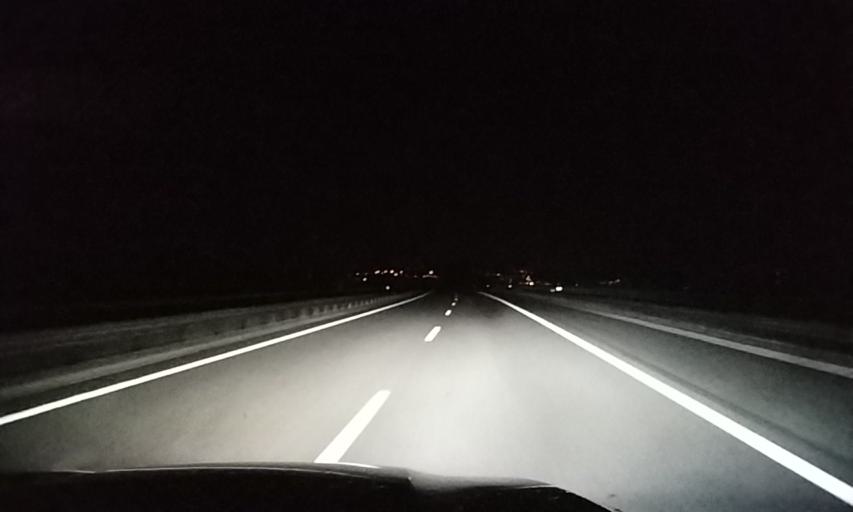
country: PT
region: Coimbra
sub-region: Coimbra
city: Coimbra
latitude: 40.2157
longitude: -8.4869
